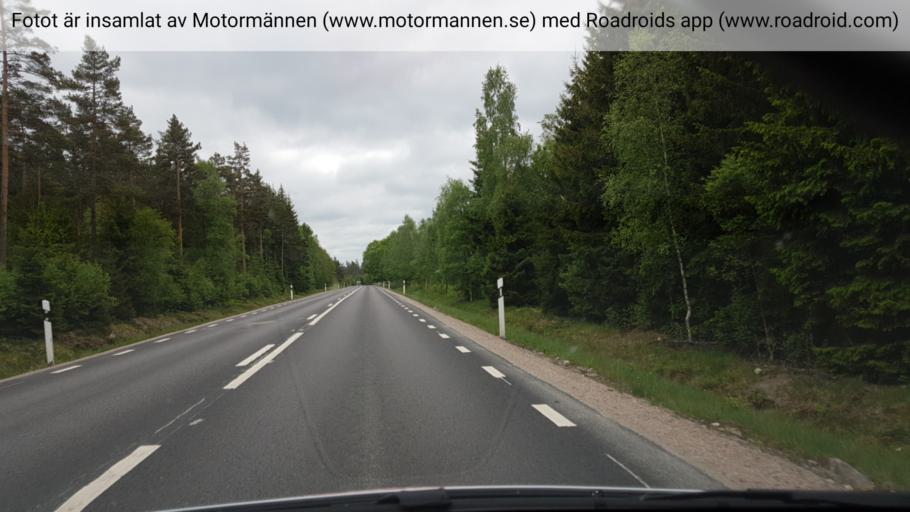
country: SE
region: Joenkoeping
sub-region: Vetlanda Kommun
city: Vetlanda
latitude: 57.2648
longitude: 15.1281
